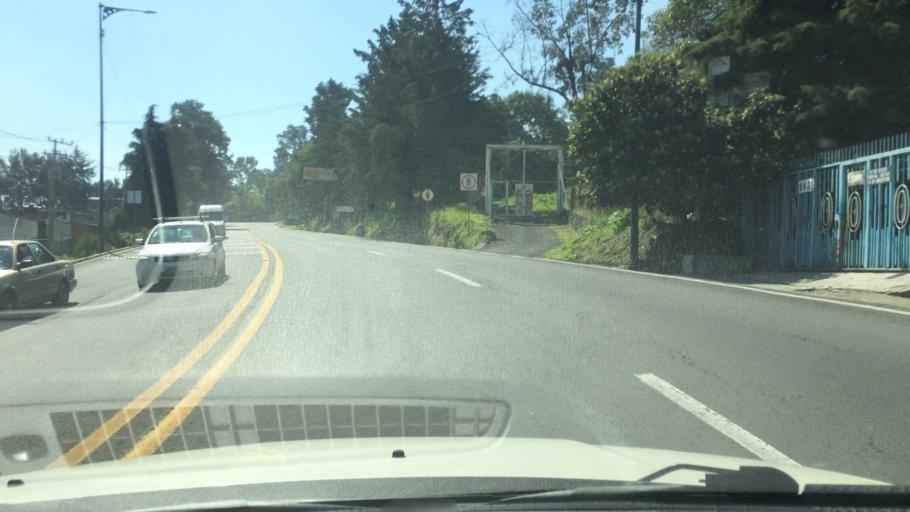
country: MX
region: Mexico City
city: Tlalpan
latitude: 19.2416
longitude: -99.1657
